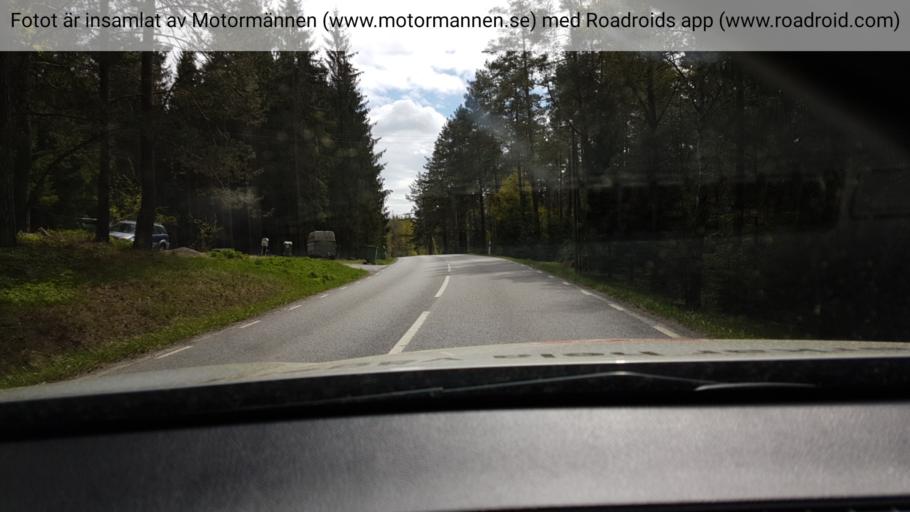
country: SE
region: Stockholm
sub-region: Haninge Kommun
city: Haninge
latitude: 59.1476
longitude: 18.1802
